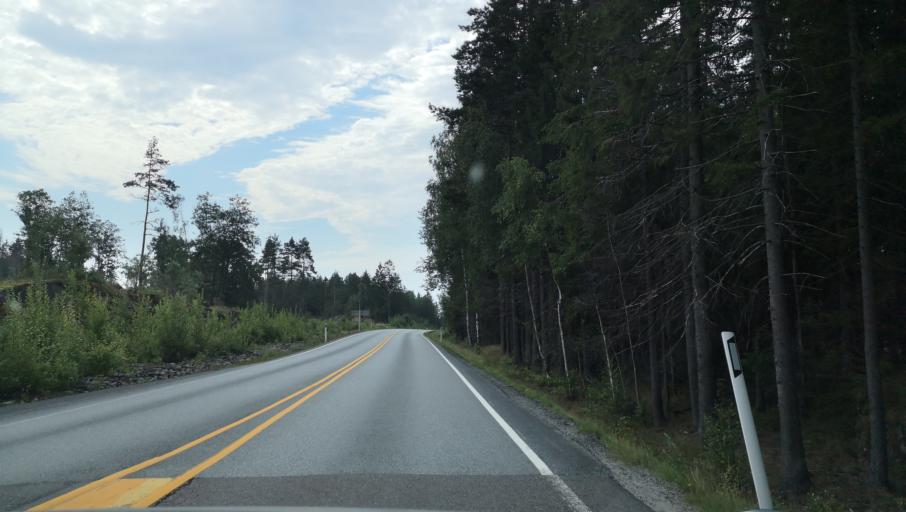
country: NO
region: Ostfold
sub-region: Valer
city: Kirkebygda
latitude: 59.4815
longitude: 10.7946
